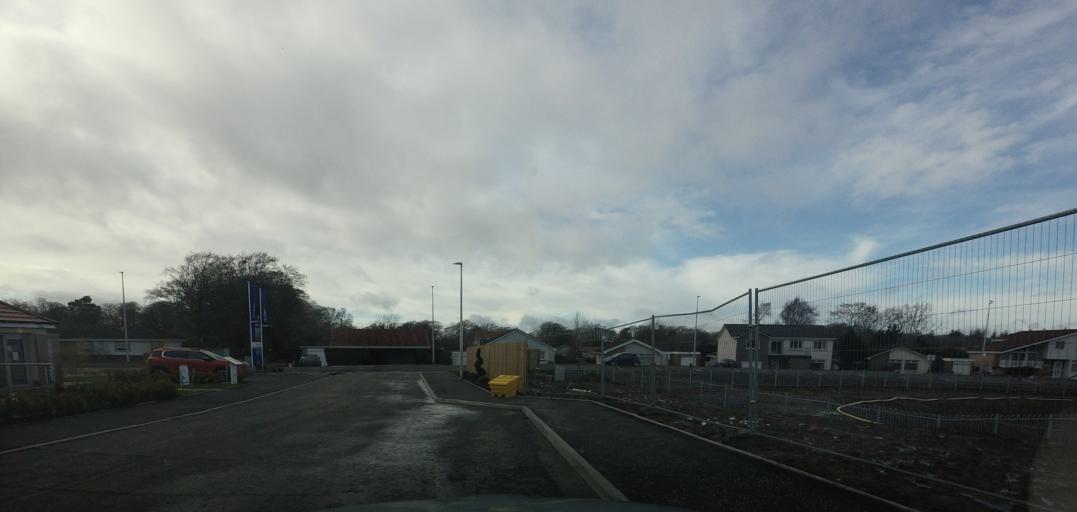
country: GB
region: Scotland
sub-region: West Lothian
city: Mid Calder
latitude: 55.8666
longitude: -3.5017
